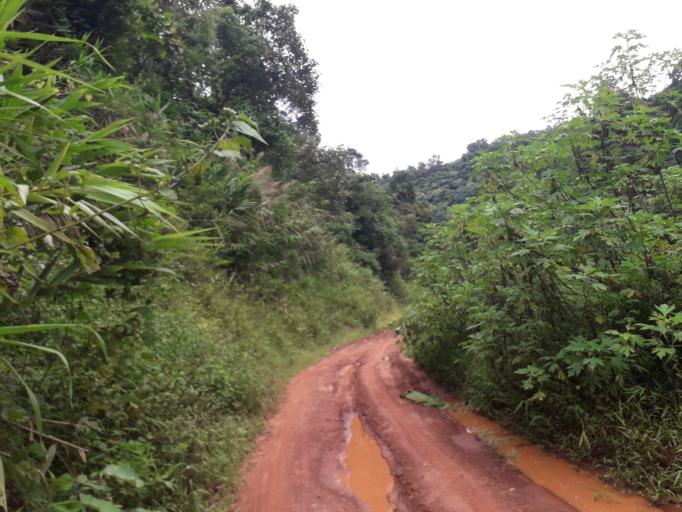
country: CN
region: Yunnan
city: Menglie
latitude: 22.1898
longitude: 101.7012
